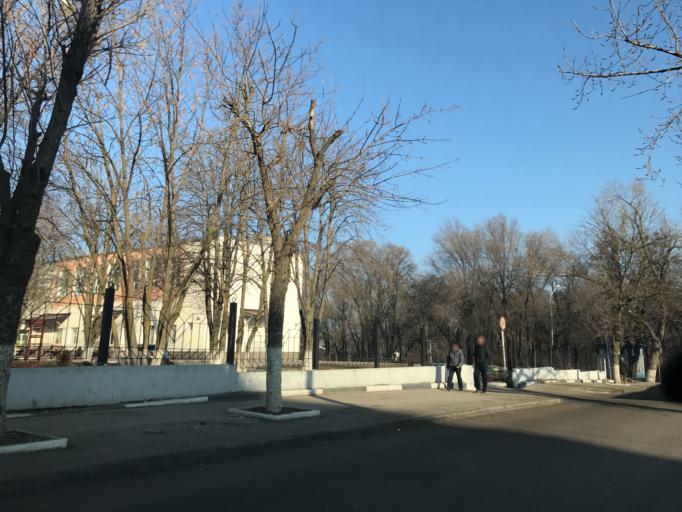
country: RU
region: Rostov
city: Rostov-na-Donu
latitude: 47.2145
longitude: 39.6751
